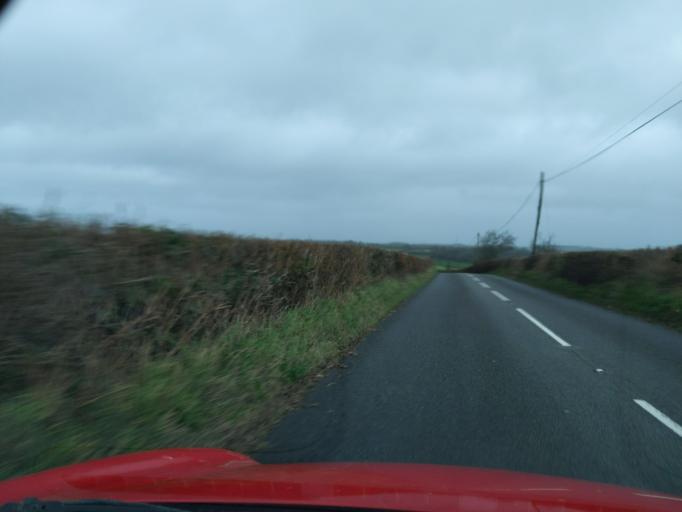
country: GB
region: England
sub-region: Cornwall
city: Boyton
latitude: 50.7240
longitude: -4.3275
